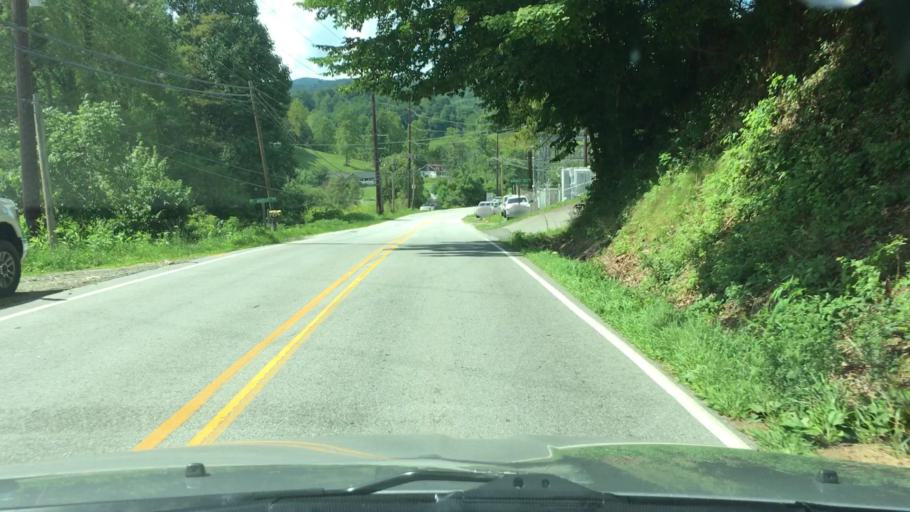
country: US
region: North Carolina
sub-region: Yancey County
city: Burnsville
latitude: 35.9045
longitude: -82.2144
